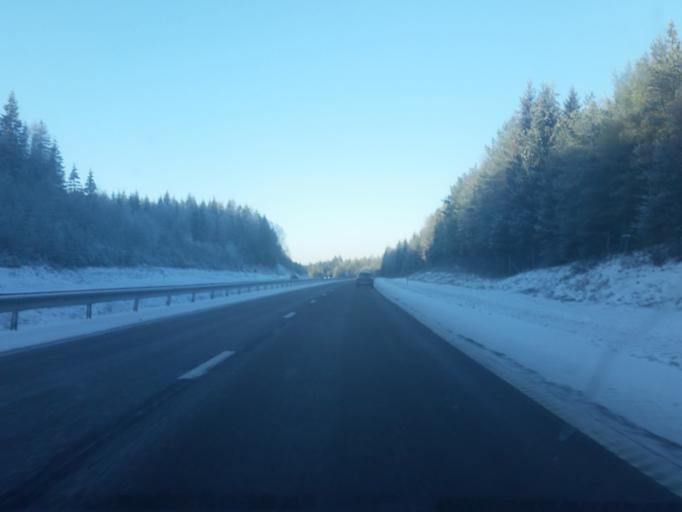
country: SE
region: Vaestra Goetaland
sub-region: Bollebygds Kommun
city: Bollebygd
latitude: 57.6705
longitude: 12.6385
